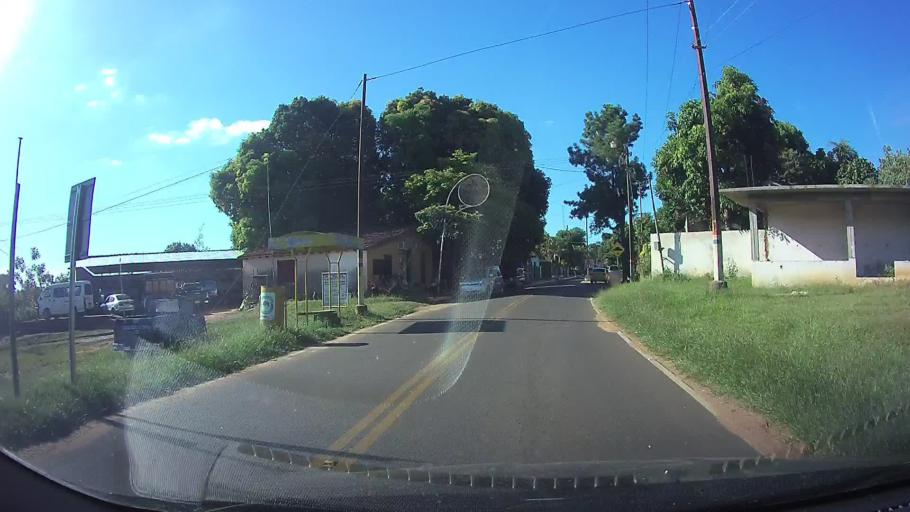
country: PY
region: Cordillera
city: Atyra
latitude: -25.2864
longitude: -57.1710
